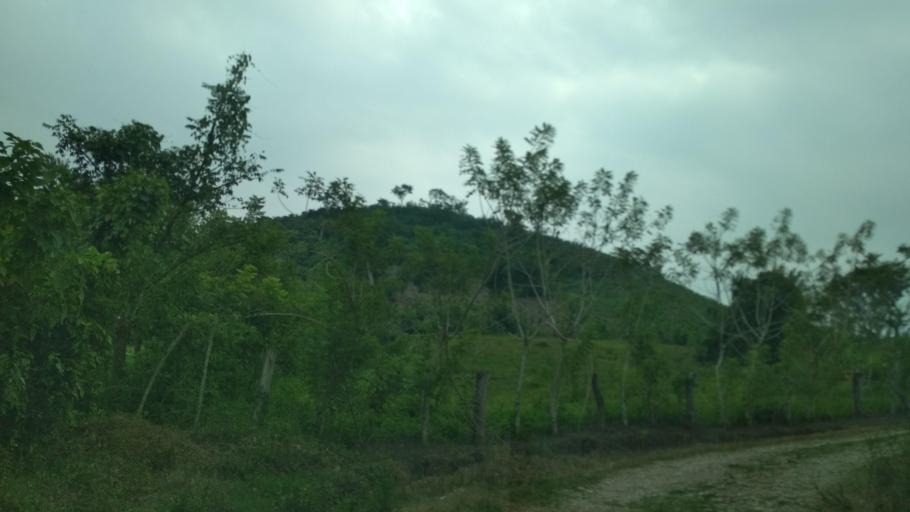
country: MM
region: Kayah
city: Loikaw
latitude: 20.2108
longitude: 97.3276
